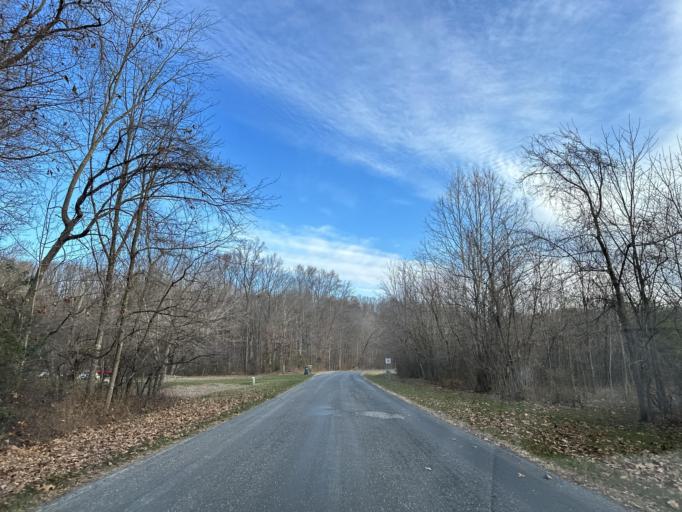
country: US
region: Virginia
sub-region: City of Staunton
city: Staunton
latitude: 38.2145
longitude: -79.2181
